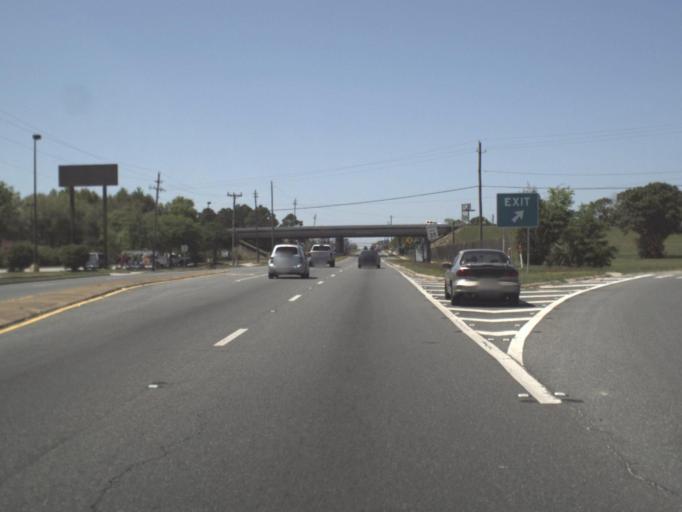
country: US
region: Florida
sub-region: Escambia County
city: West Pensacola
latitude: 30.4290
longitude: -87.2707
